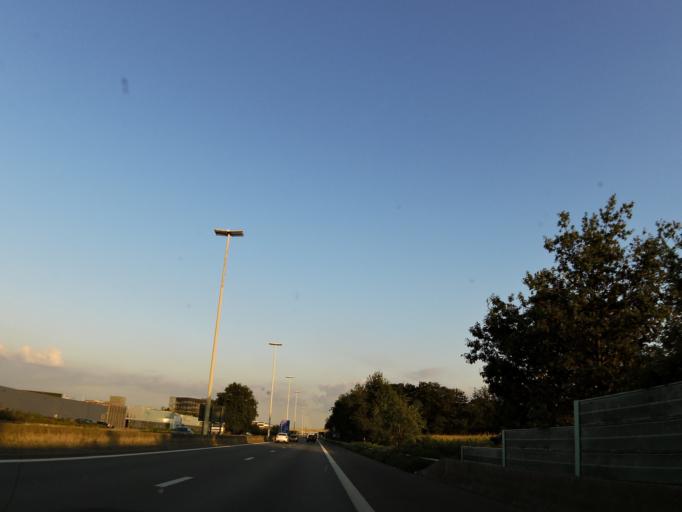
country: BE
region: Flanders
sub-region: Provincie Antwerpen
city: Westerlo
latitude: 51.1370
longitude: 4.9193
